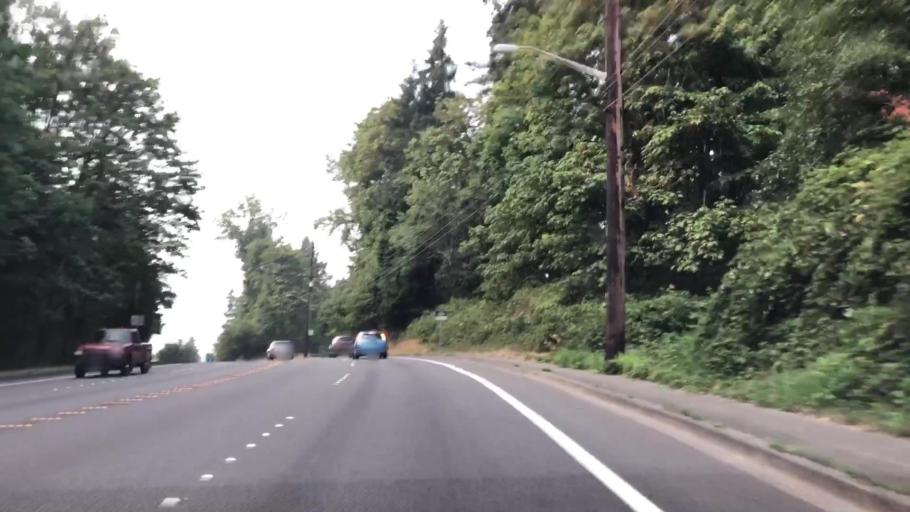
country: US
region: Washington
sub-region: King County
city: Newport
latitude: 47.5616
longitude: -122.1692
